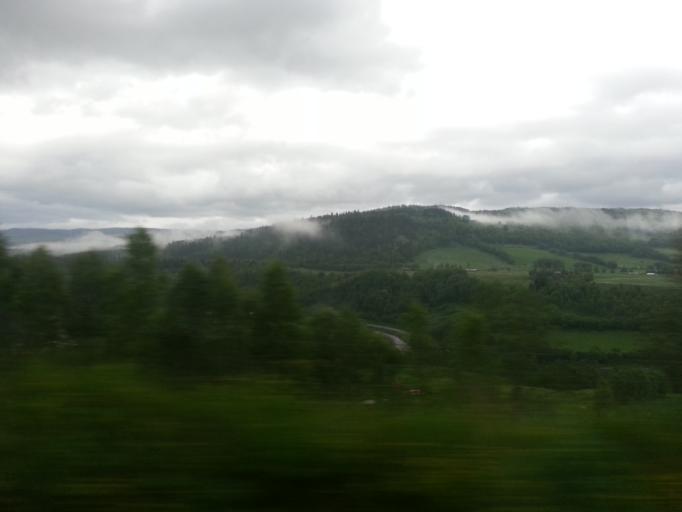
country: NO
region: Sor-Trondelag
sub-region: Midtre Gauldal
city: Storen
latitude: 62.9634
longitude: 10.1759
